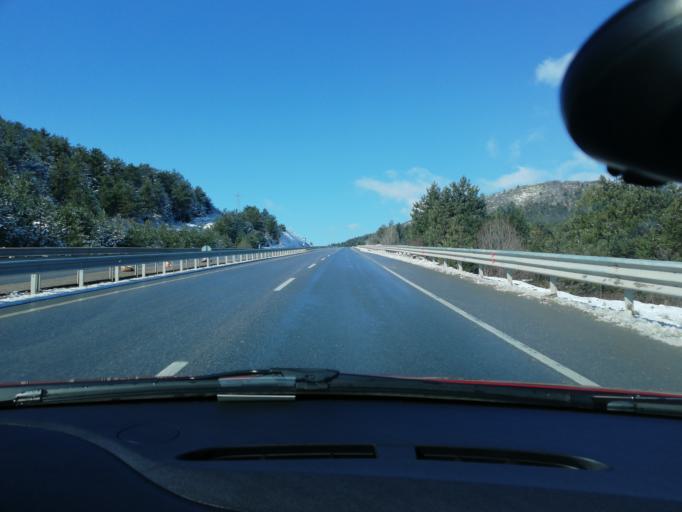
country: TR
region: Kastamonu
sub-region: Cide
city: Kastamonu
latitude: 41.3602
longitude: 33.7033
